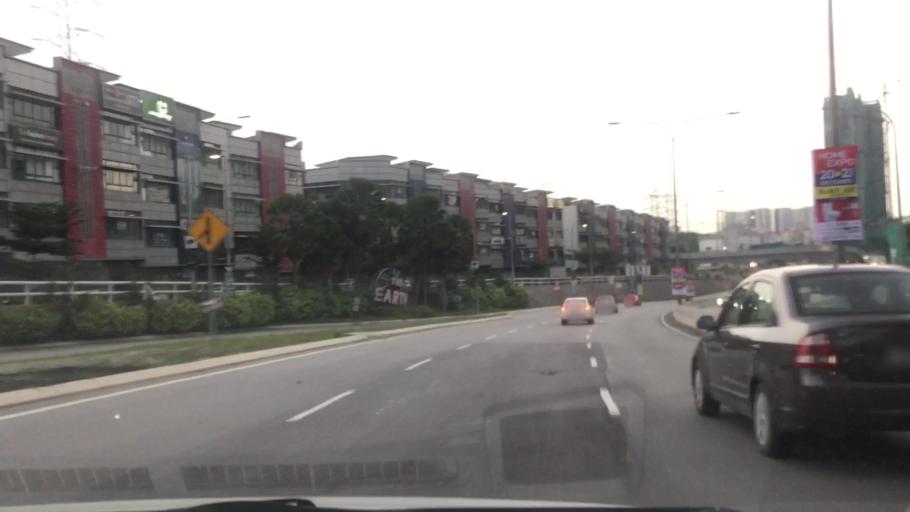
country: MY
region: Selangor
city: Kampong Baharu Balakong
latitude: 3.0493
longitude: 101.6706
